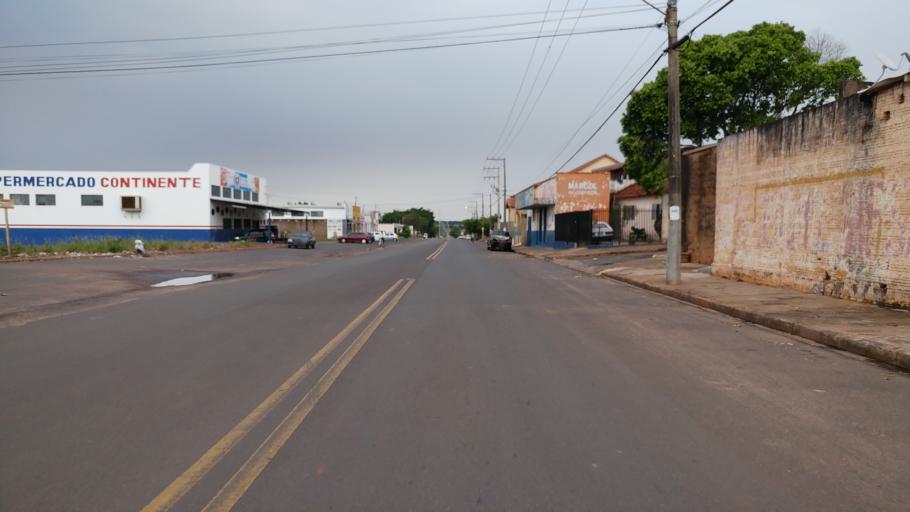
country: BR
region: Sao Paulo
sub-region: Paraguacu Paulista
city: Paraguacu Paulista
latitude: -22.4313
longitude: -50.5791
